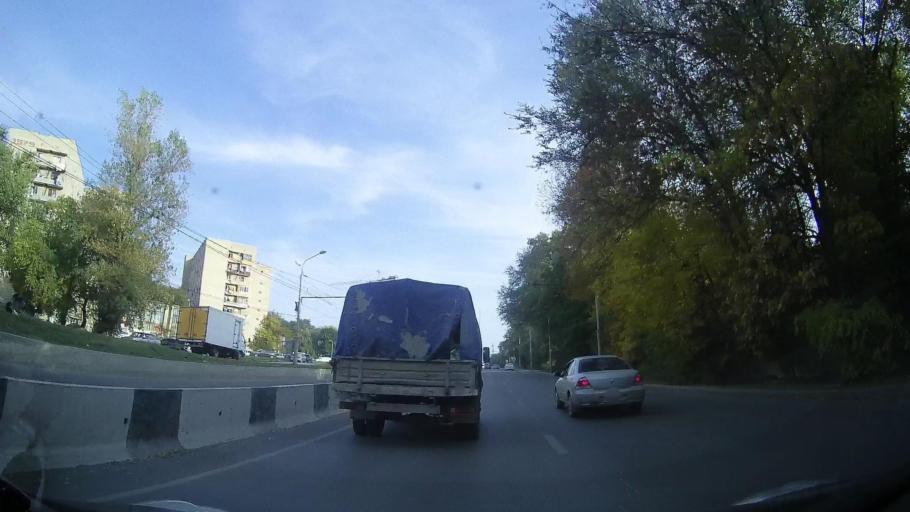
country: RU
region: Rostov
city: Temernik
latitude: 47.2890
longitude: 39.7399
